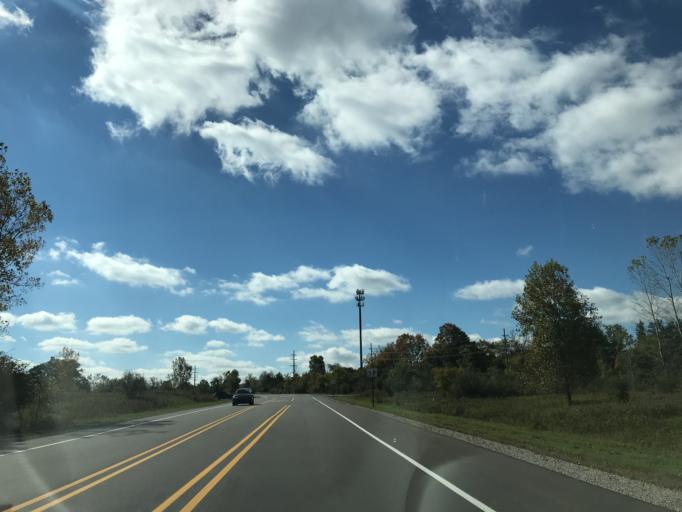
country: US
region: Michigan
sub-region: Washtenaw County
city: Ann Arbor
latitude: 42.2983
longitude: -83.6808
